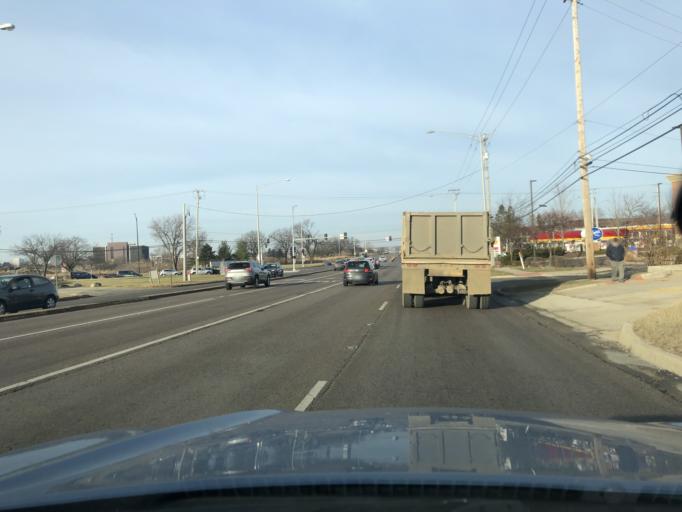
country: US
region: Illinois
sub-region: Cook County
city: Rolling Meadows
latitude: 42.0679
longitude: -88.0417
